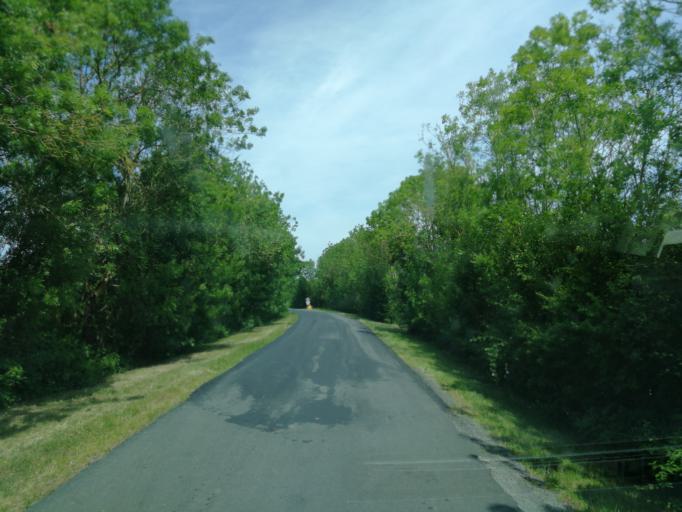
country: FR
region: Pays de la Loire
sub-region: Departement de la Vendee
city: Le Langon
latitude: 46.4010
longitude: -0.9288
